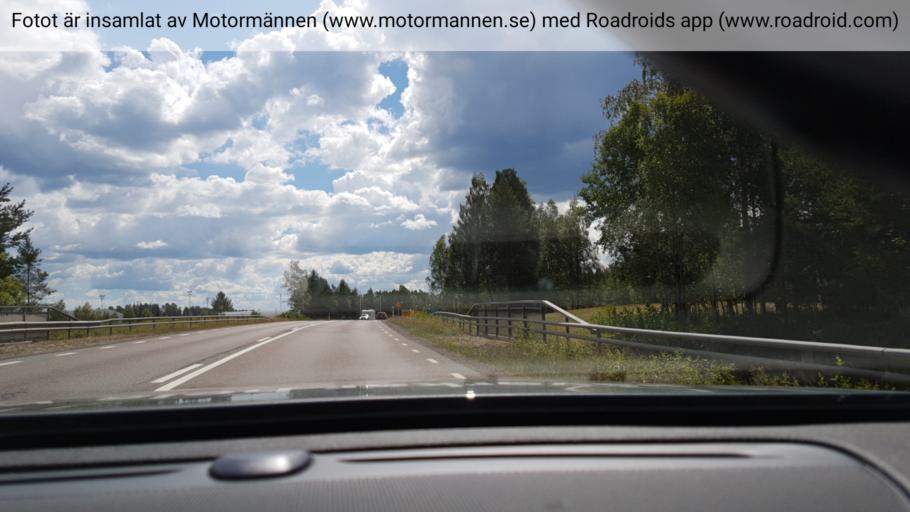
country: SE
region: Dalarna
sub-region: Faluns Kommun
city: Falun
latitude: 60.6216
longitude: 15.6454
